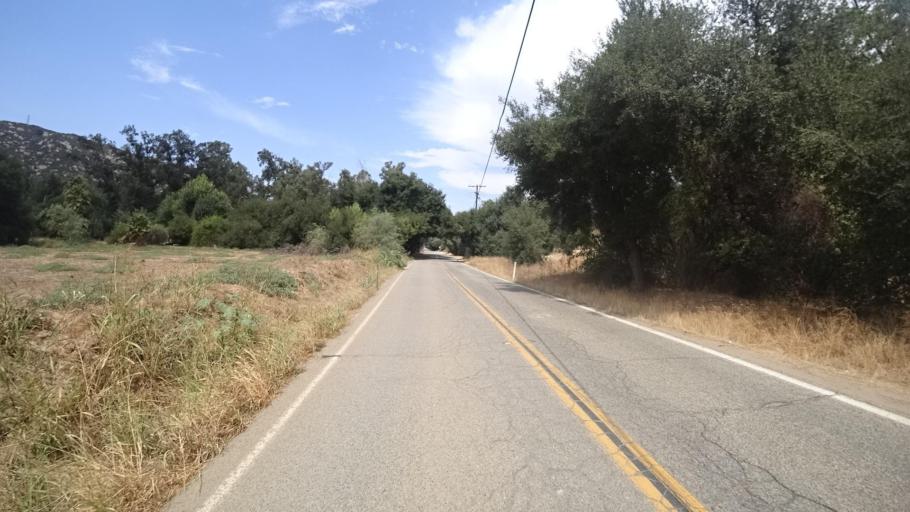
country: US
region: California
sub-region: San Diego County
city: Hidden Meadows
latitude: 33.1957
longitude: -117.0890
